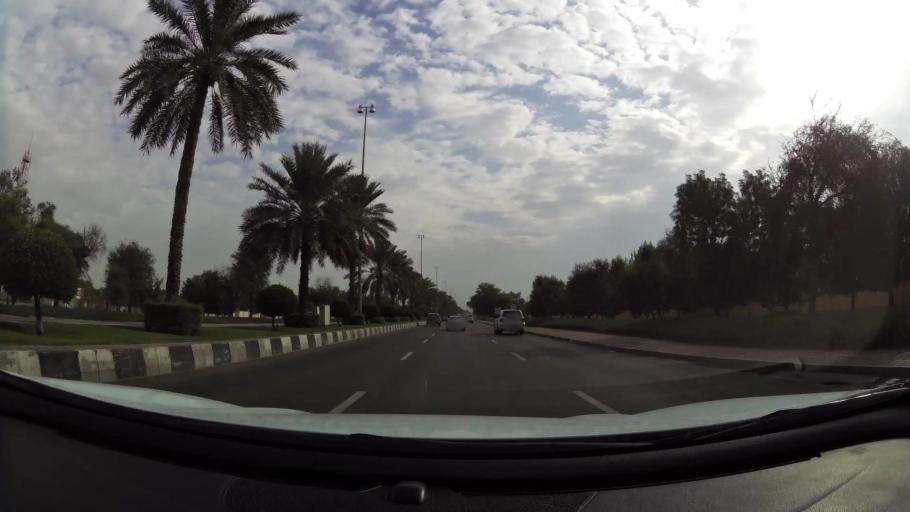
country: AE
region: Abu Dhabi
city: Al Ain
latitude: 24.1872
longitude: 55.6379
